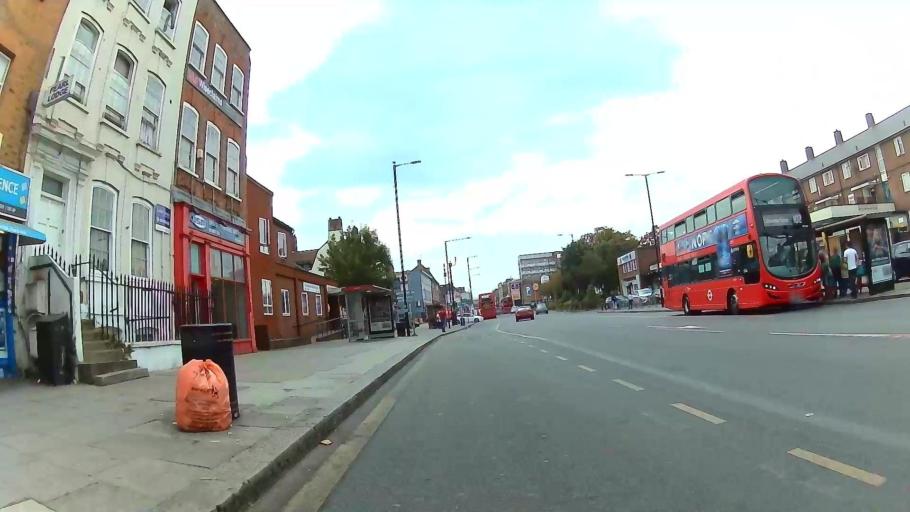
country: GB
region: England
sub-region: Greater London
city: Enfield
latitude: 51.6163
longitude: -0.0639
